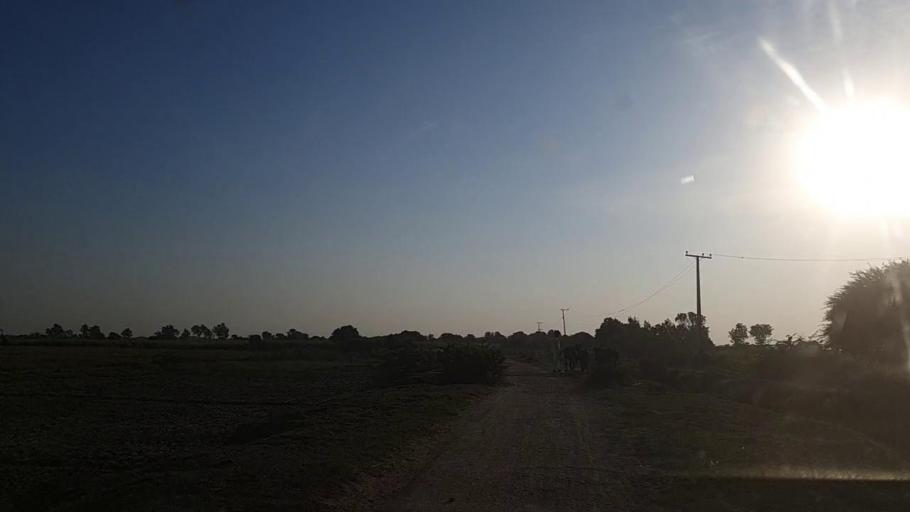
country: PK
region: Sindh
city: Mirpur Batoro
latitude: 24.6801
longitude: 68.2166
